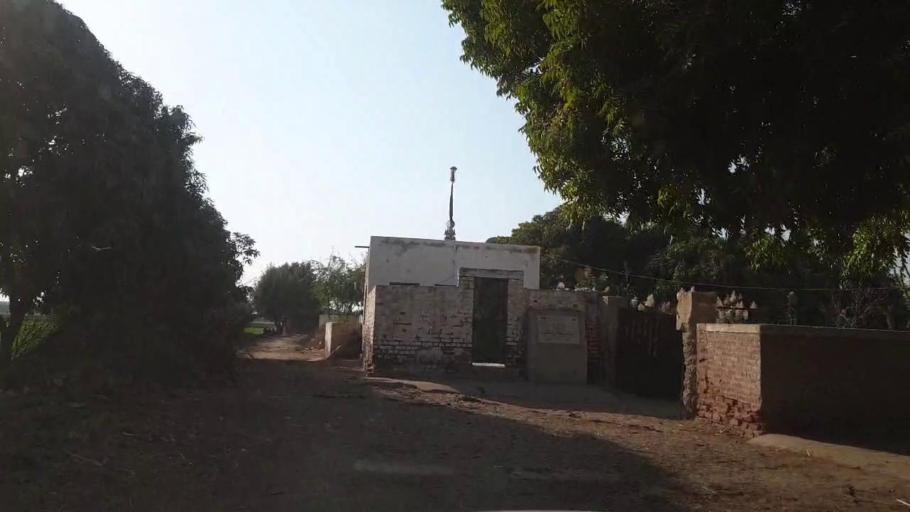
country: PK
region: Sindh
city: Tando Allahyar
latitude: 25.5654
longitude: 68.6504
